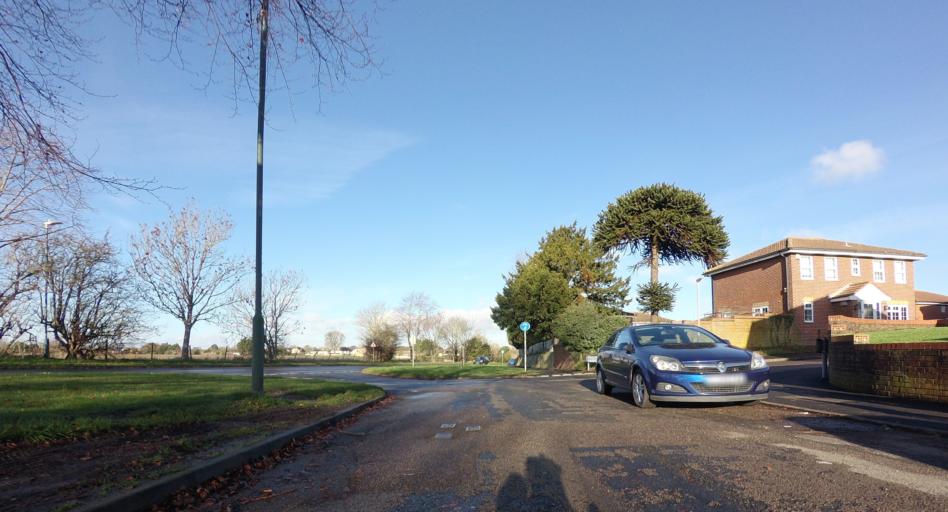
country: GB
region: England
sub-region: Kent
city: Dartford
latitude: 51.4244
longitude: 0.2016
